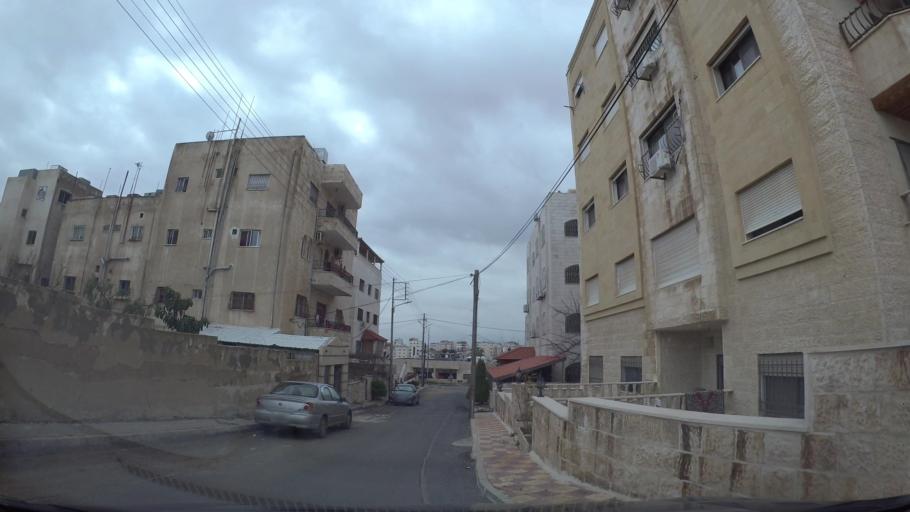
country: JO
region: Amman
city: Wadi as Sir
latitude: 31.9632
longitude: 35.8343
